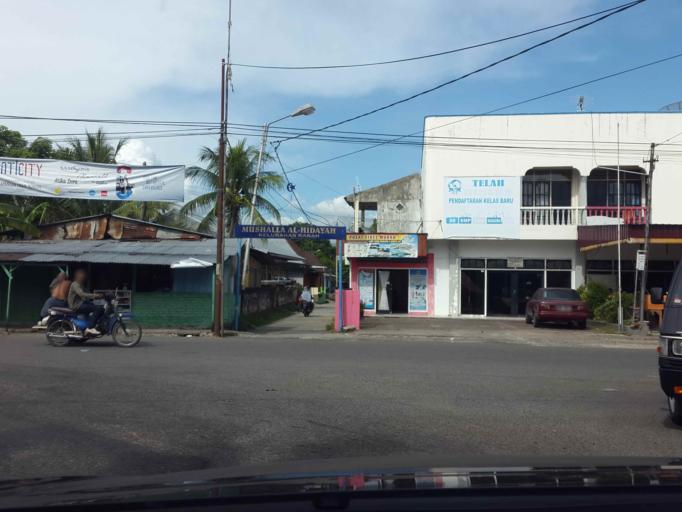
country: ID
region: West Sumatra
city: Padang
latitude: -0.9570
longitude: 100.3686
